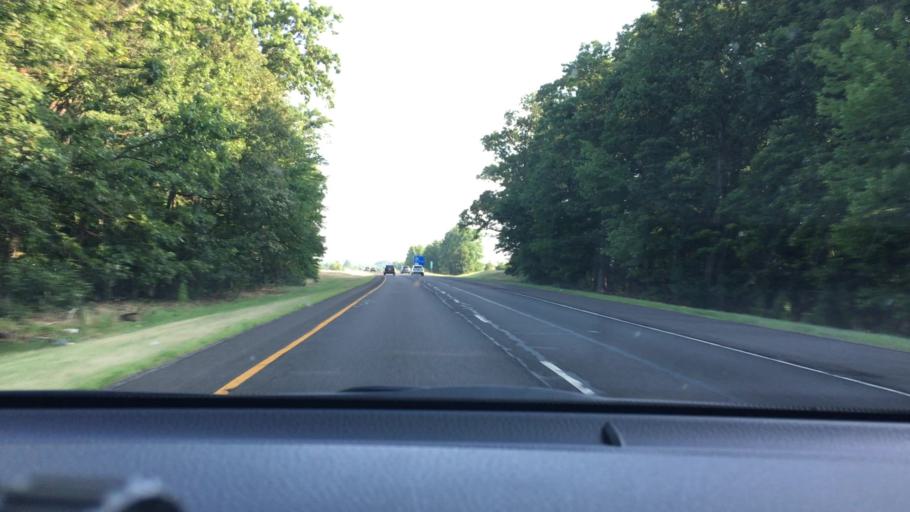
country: US
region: New Jersey
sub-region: Gloucester County
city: Richwood
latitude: 39.7055
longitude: -75.1521
